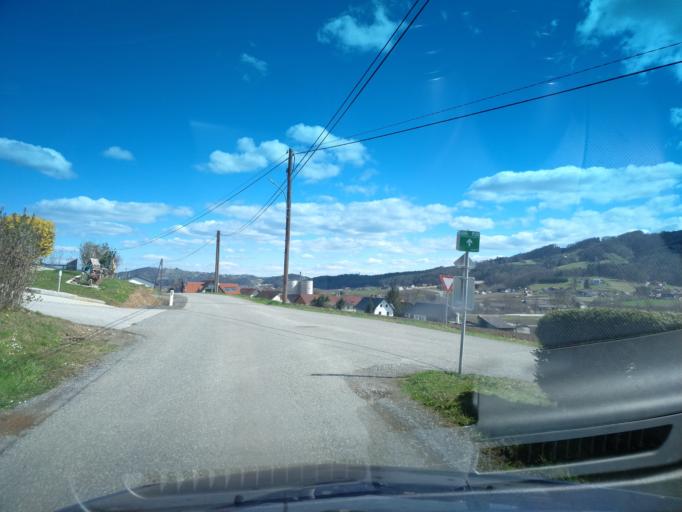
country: AT
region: Styria
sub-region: Politischer Bezirk Leibnitz
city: Sankt Johann im Saggautal
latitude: 46.7203
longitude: 15.4006
